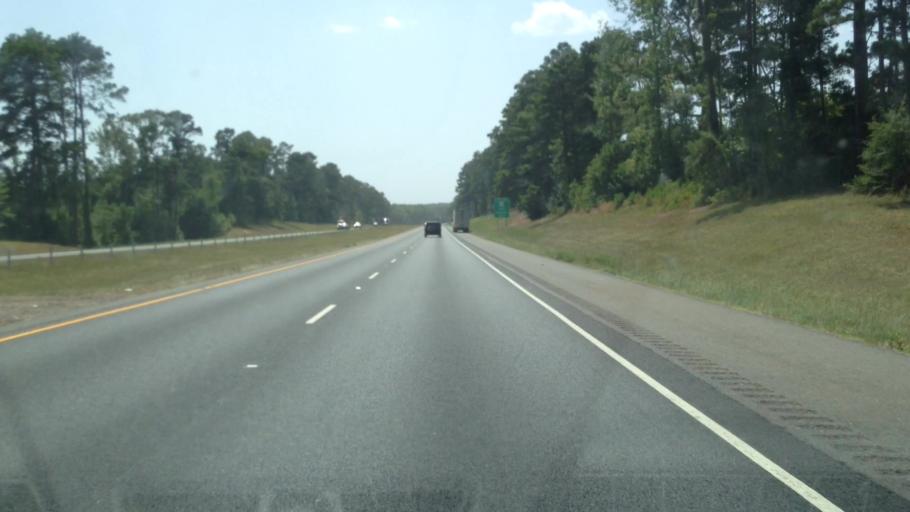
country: US
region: Louisiana
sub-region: Webster Parish
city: Minden
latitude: 32.5622
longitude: -93.1357
